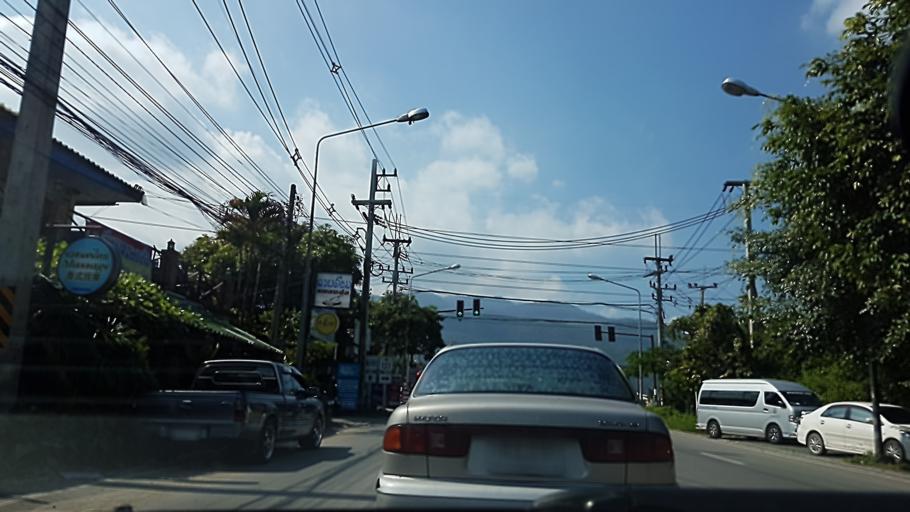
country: TH
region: Chiang Mai
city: Chiang Mai
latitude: 18.8226
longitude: 98.9660
